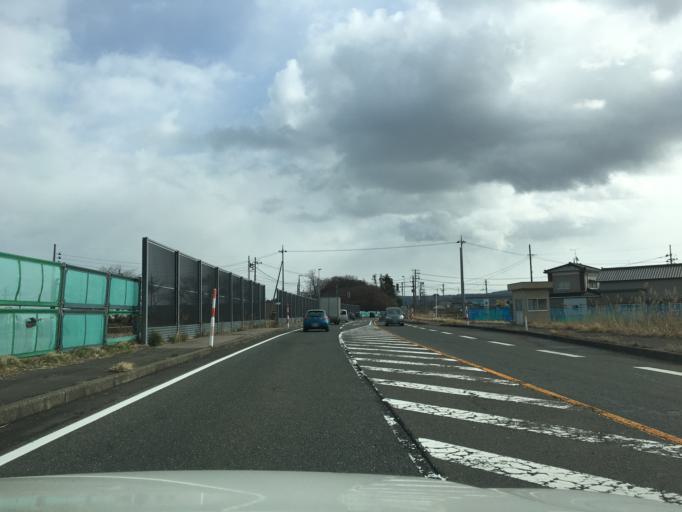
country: JP
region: Yamagata
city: Yuza
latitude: 39.2775
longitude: 139.9278
